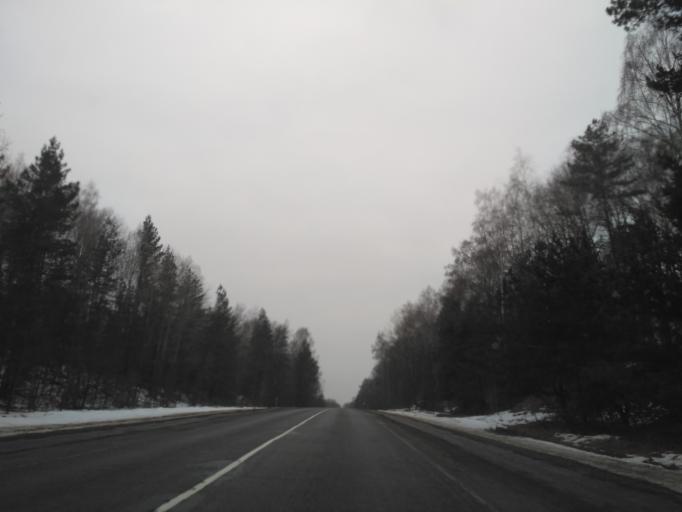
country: BY
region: Brest
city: Lyakhavichy
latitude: 53.2279
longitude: 26.1938
